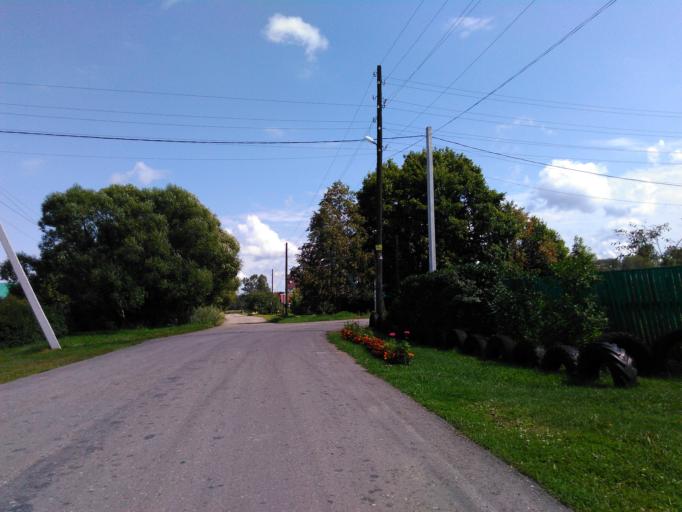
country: RU
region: Vladimir
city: Krasnyy Oktyabr'
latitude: 56.0214
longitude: 38.8050
